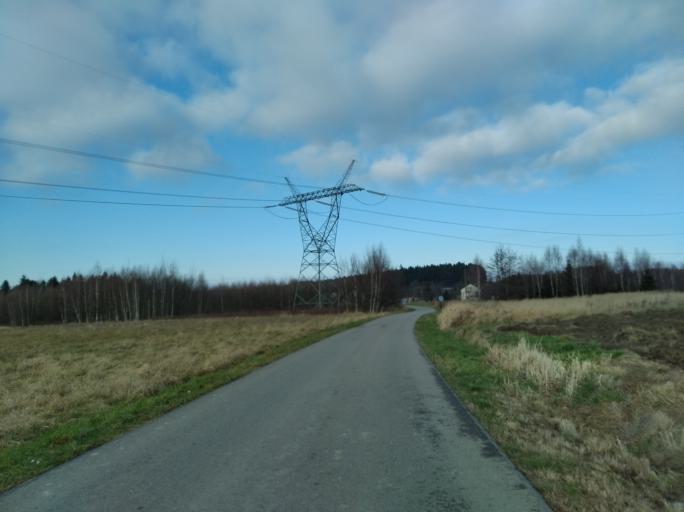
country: PL
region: Subcarpathian Voivodeship
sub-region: Powiat strzyzowski
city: Babica
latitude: 49.9033
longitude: 21.8514
